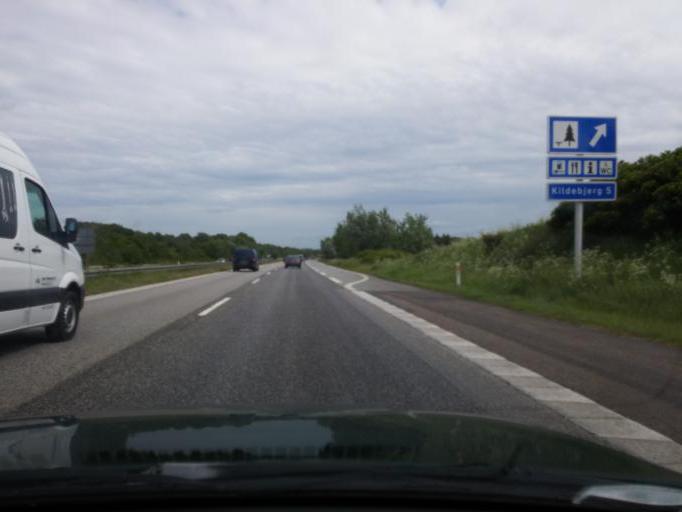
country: DK
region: South Denmark
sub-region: Assens Kommune
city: Vissenbjerg
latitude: 55.3967
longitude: 10.1788
